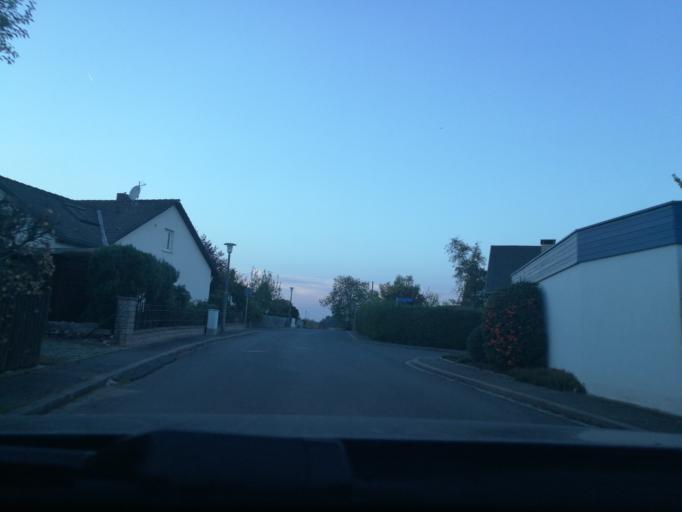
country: DE
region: Bavaria
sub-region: Regierungsbezirk Mittelfranken
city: Seukendorf
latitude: 49.4909
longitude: 10.8738
